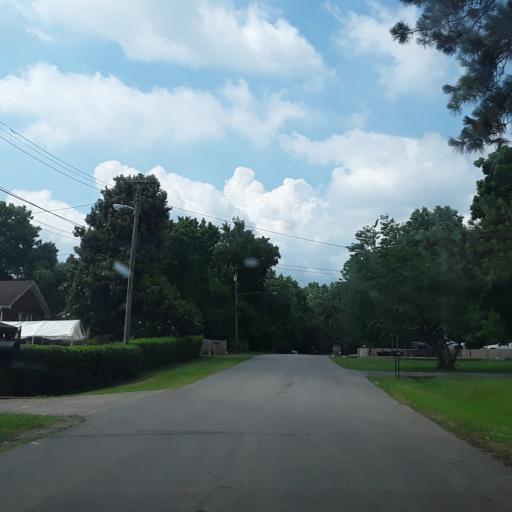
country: US
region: Tennessee
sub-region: Davidson County
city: Oak Hill
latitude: 36.1147
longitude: -86.7223
